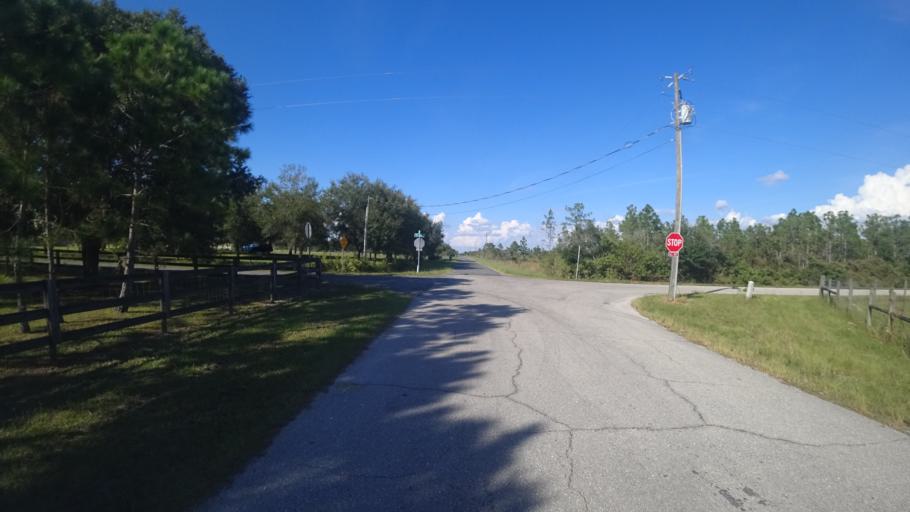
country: US
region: Florida
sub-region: Sarasota County
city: Fruitville
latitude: 27.4049
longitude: -82.2834
